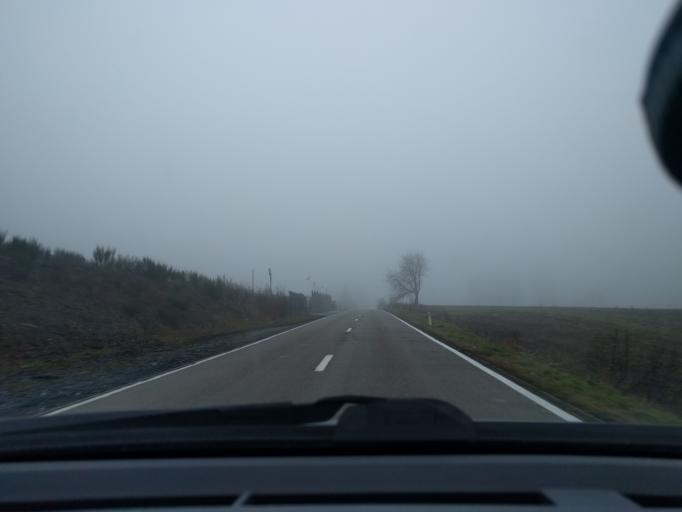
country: BE
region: Wallonia
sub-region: Province du Luxembourg
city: Gouvy
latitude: 50.2014
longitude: 5.9221
